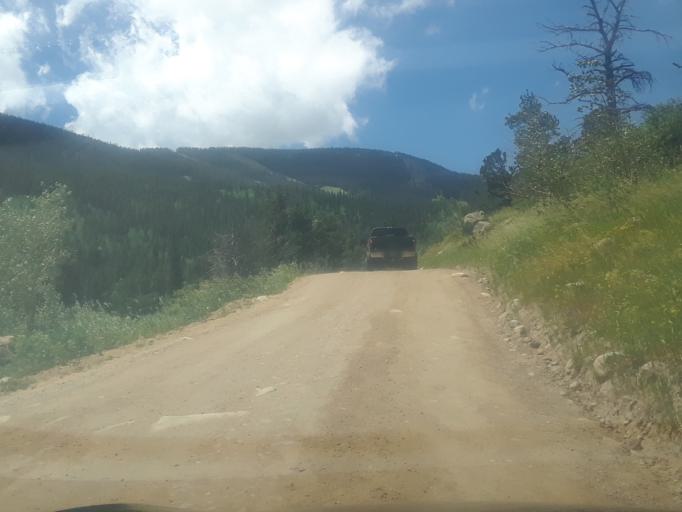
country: US
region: Colorado
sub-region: Boulder County
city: Nederland
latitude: 39.9502
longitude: -105.5883
